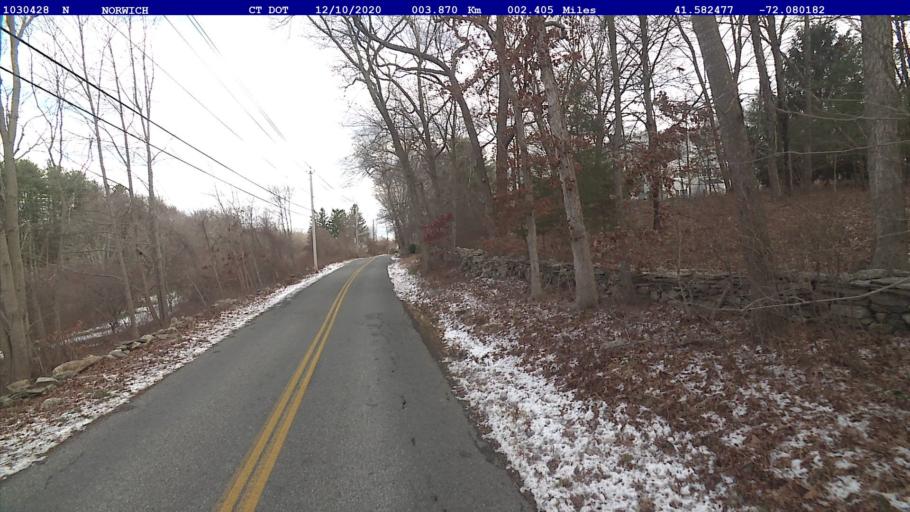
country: US
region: Connecticut
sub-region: New London County
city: Baltic
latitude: 41.5825
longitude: -72.0802
